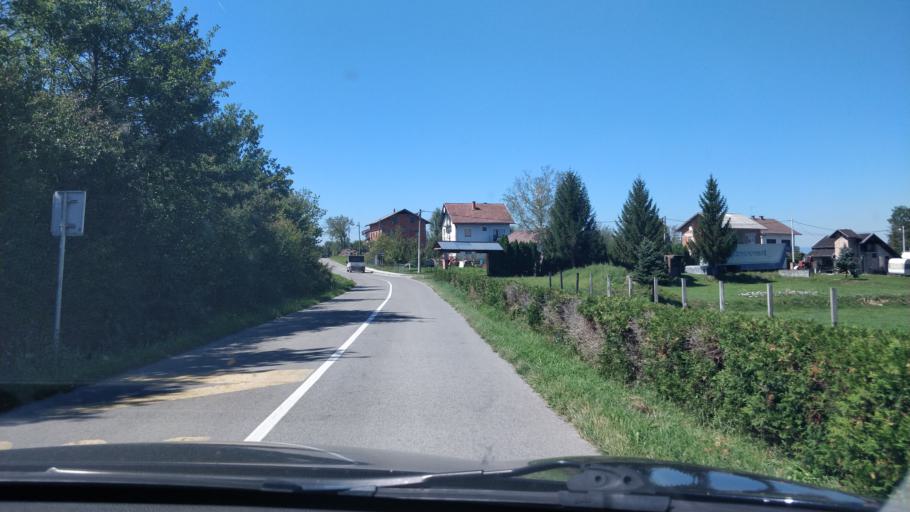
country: HR
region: Karlovacka
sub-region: Grad Karlovac
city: Karlovac
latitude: 45.4709
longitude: 15.6191
